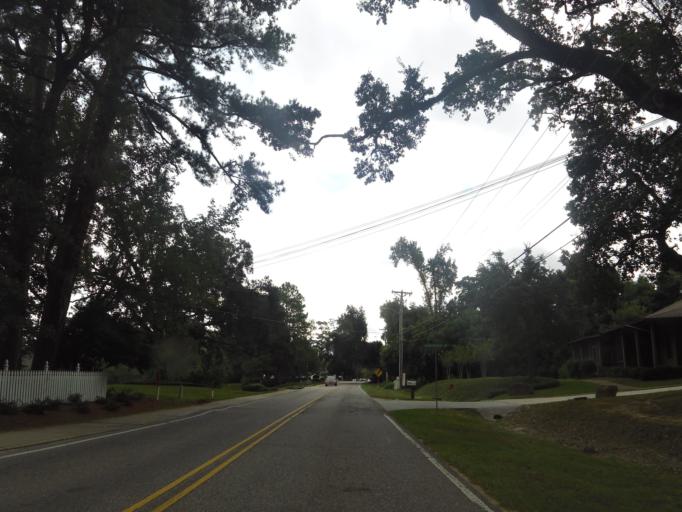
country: US
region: Alabama
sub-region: Baldwin County
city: Fairhope
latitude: 30.5111
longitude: -87.9188
